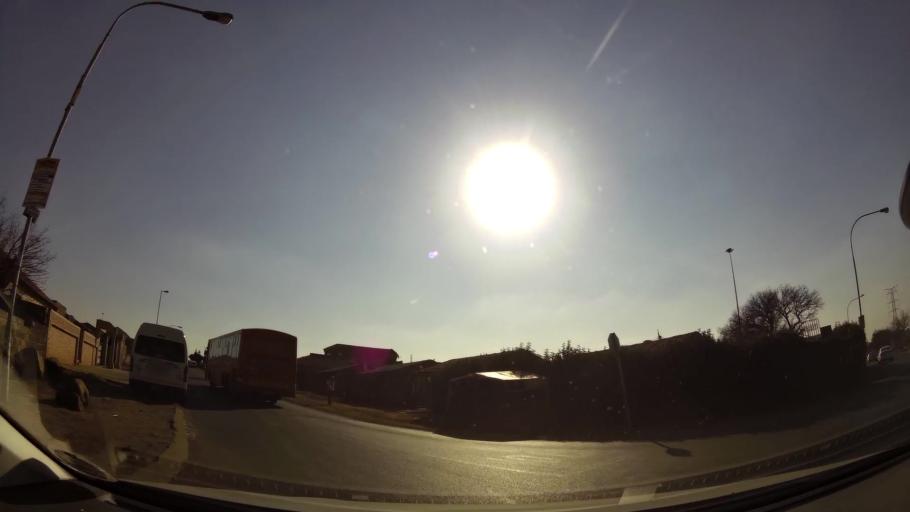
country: ZA
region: Gauteng
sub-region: City of Johannesburg Metropolitan Municipality
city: Soweto
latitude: -26.2741
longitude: 27.8814
